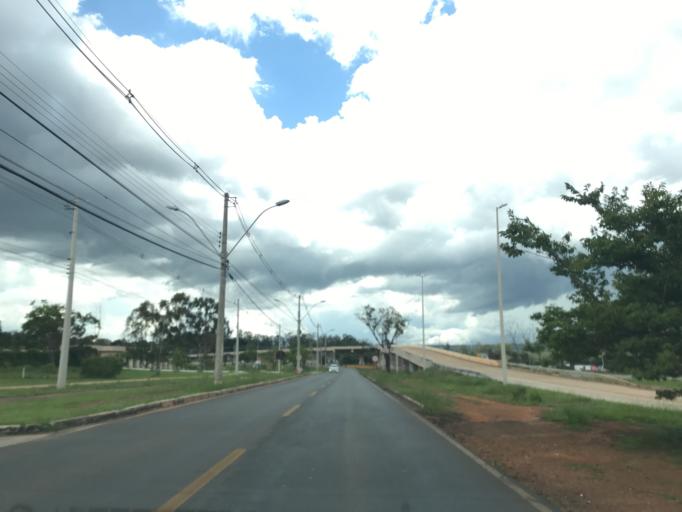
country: BR
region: Federal District
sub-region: Brasilia
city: Brasilia
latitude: -15.8752
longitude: -47.9566
